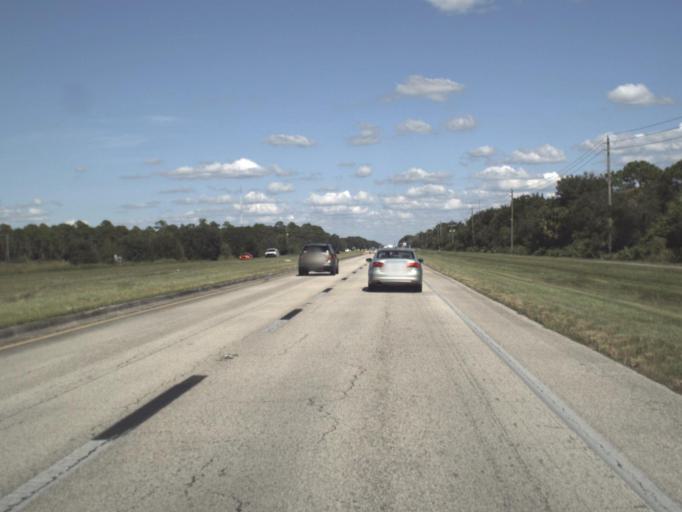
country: US
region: Florida
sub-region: Sarasota County
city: North Port
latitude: 26.9961
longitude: -82.1950
